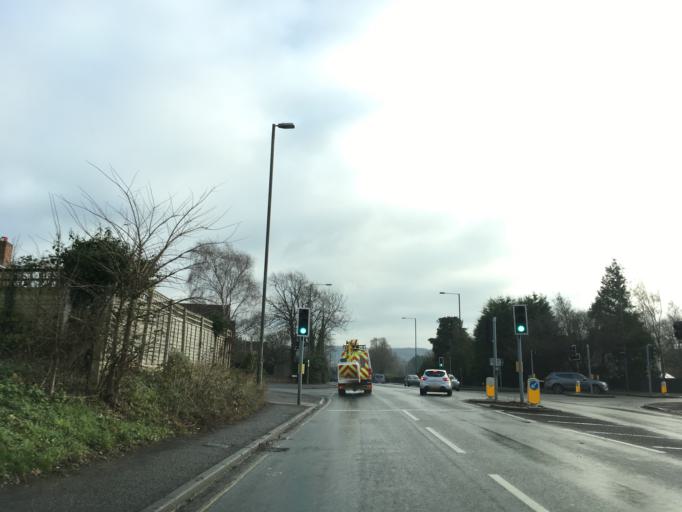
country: GB
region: England
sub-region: Gloucestershire
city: Churchdown
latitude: 51.8488
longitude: -2.1681
